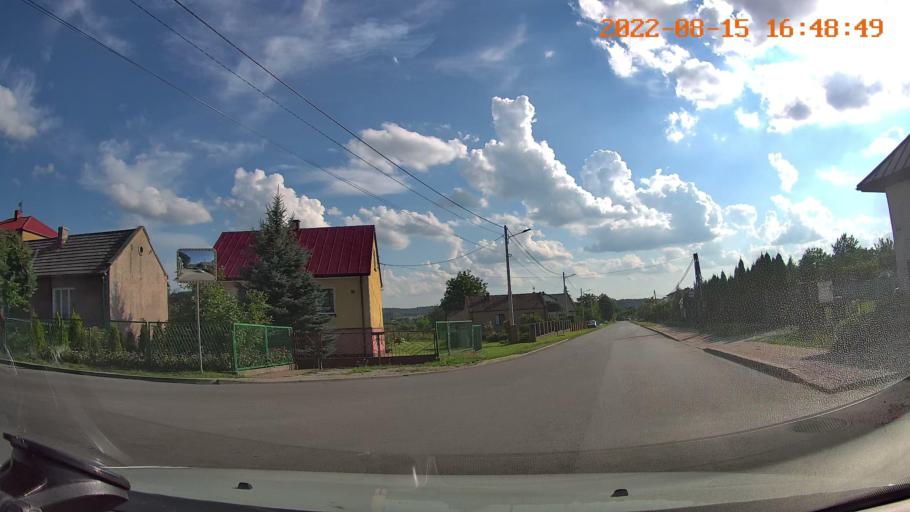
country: PL
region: Swietokrzyskie
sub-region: Powiat kielecki
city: Piekoszow
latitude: 50.8800
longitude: 20.4600
